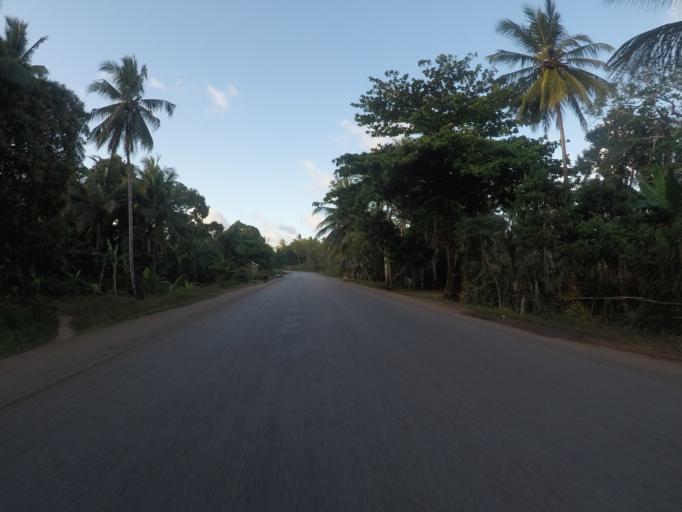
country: TZ
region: Zanzibar Central/South
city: Koani
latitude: -6.1808
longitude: 39.3279
